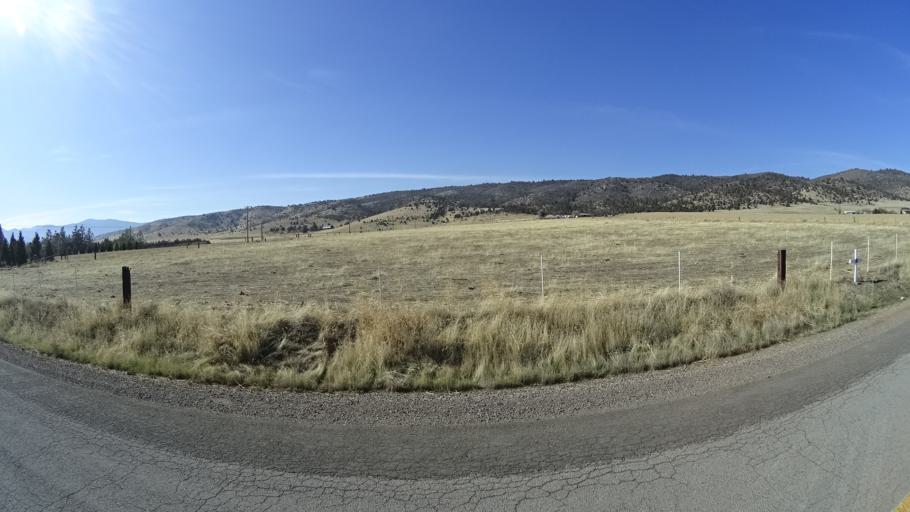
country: US
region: California
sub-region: Siskiyou County
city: Montague
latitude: 41.5860
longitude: -122.5443
